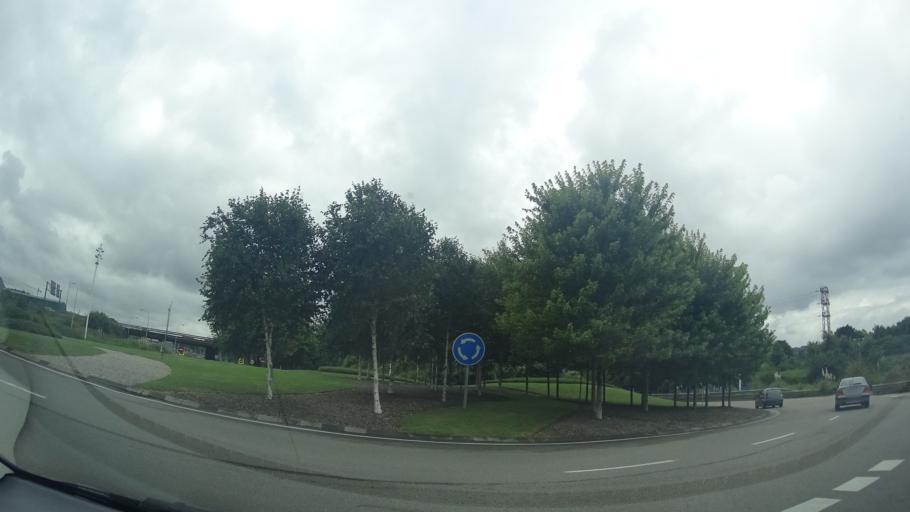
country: ES
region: Asturias
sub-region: Province of Asturias
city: Natahoyo
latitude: 43.5337
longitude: -5.6803
